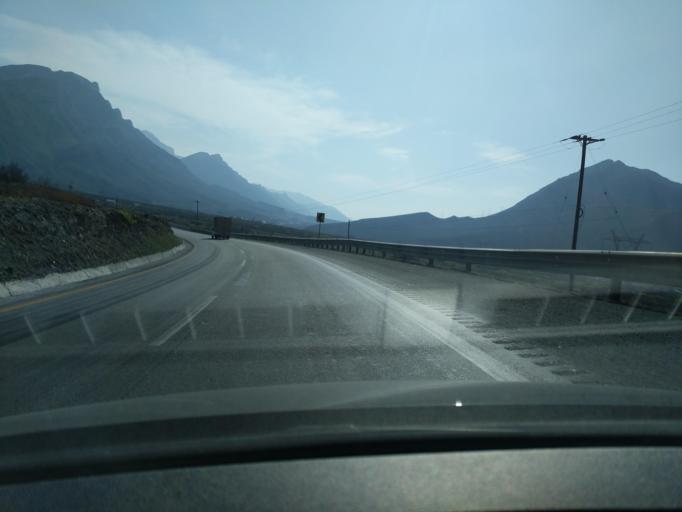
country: MX
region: Nuevo Leon
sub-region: Garcia
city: Las Torres de Guadalupe
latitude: 25.6680
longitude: -100.7053
